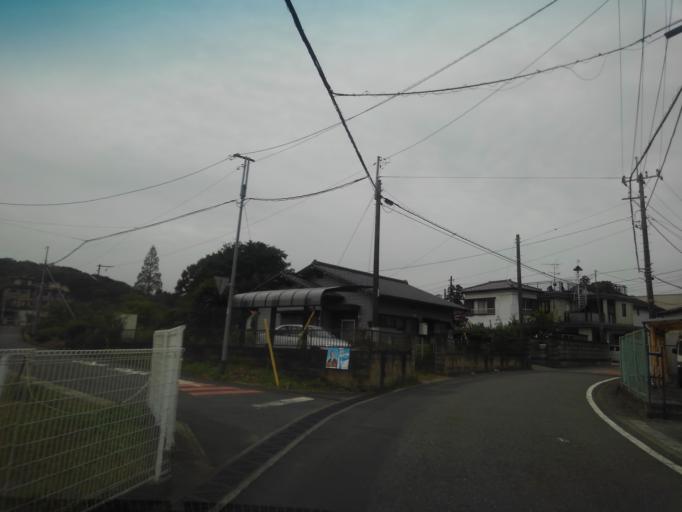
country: JP
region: Saitama
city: Sayama
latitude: 35.7897
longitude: 139.3783
